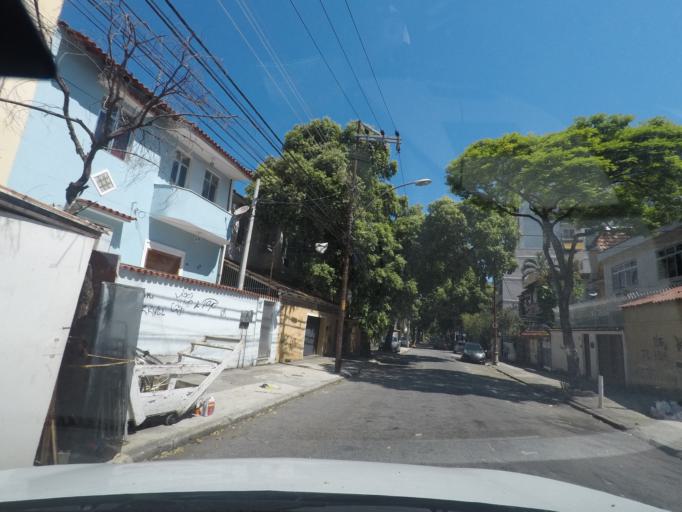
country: BR
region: Rio de Janeiro
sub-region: Rio De Janeiro
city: Rio de Janeiro
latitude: -22.9132
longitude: -43.2484
